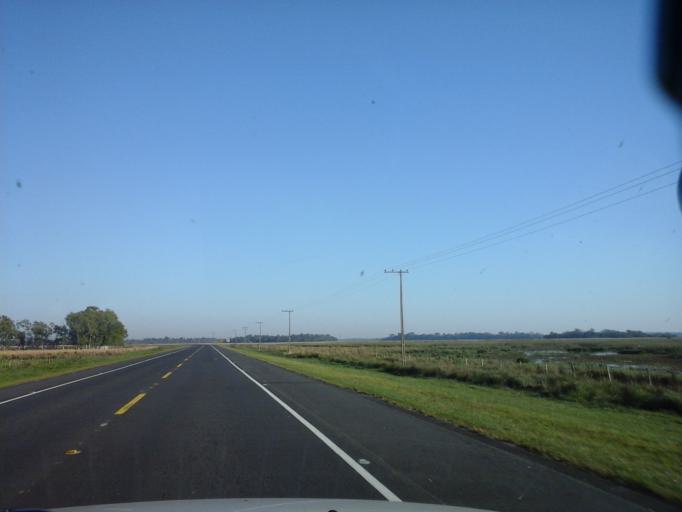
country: PY
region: Neembucu
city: Pilar
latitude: -26.8639
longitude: -57.9415
